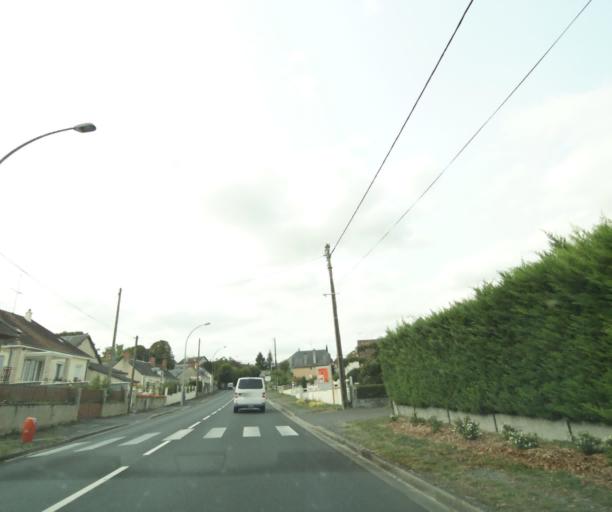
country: FR
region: Centre
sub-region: Departement de l'Indre
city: Chatillon-sur-Indre
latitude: 46.9802
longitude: 1.1777
